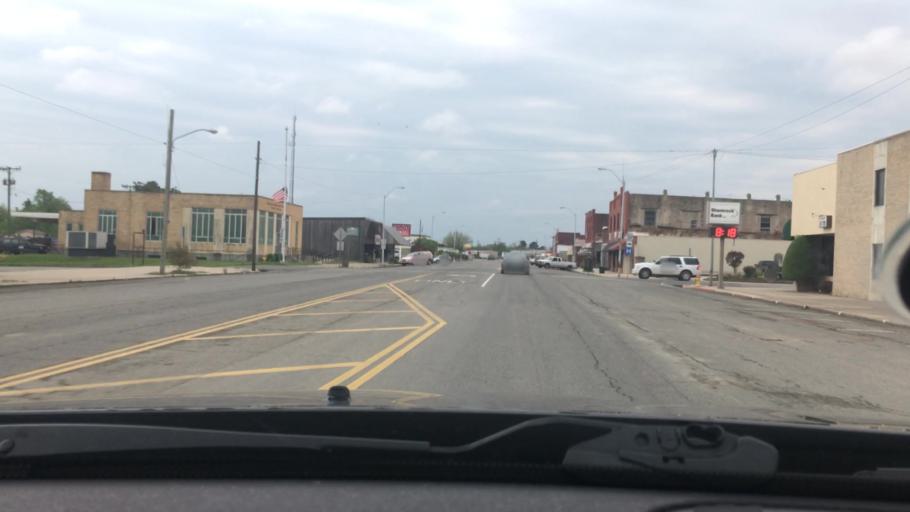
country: US
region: Oklahoma
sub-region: Coal County
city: Coalgate
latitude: 34.5401
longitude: -96.2181
